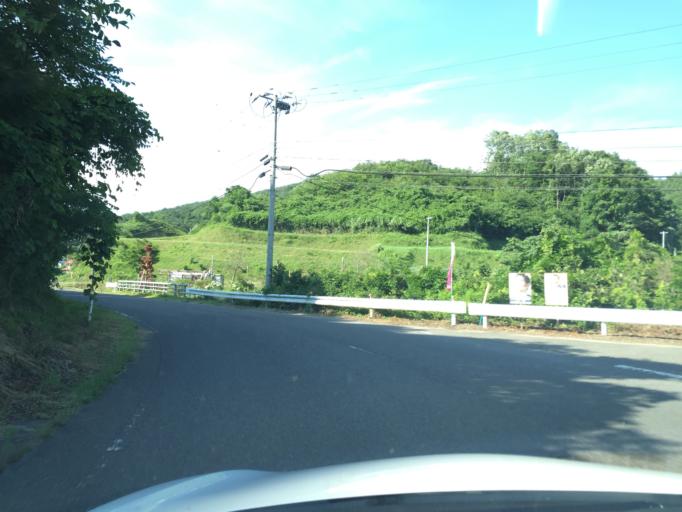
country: JP
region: Fukushima
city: Ishikawa
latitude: 37.2343
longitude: 140.4940
